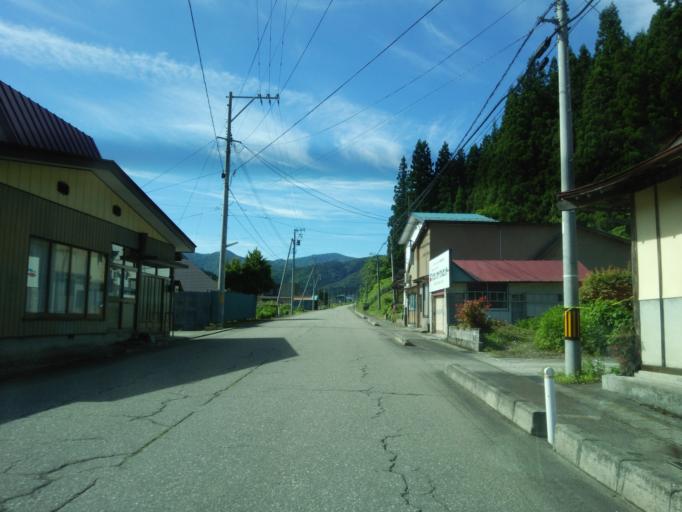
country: JP
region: Fukushima
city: Kitakata
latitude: 37.3994
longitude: 139.8146
